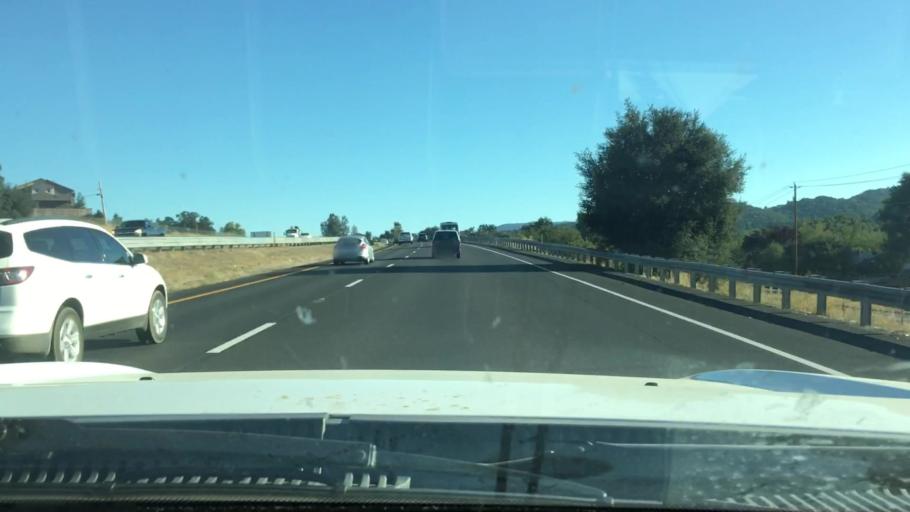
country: US
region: California
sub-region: San Luis Obispo County
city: Templeton
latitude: 35.5285
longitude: -120.7046
